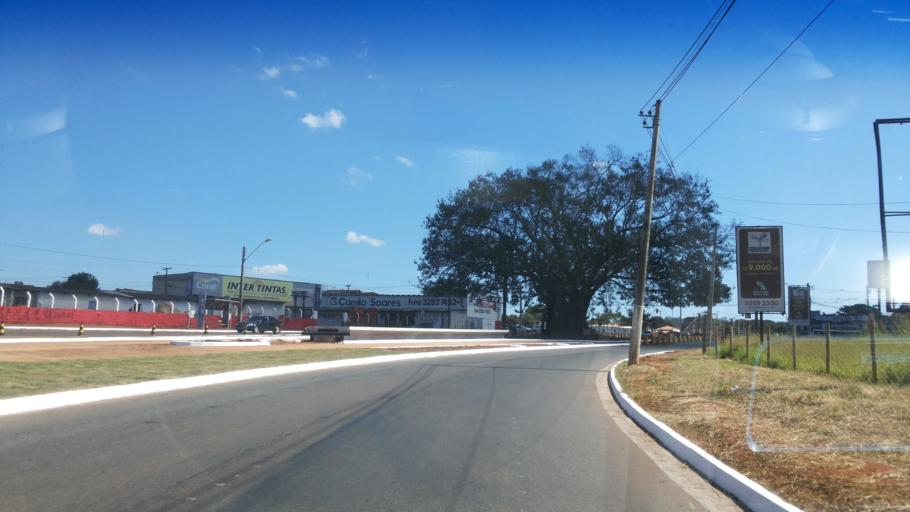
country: BR
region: Goias
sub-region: Goiania
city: Goiania
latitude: -16.6248
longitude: -49.2827
